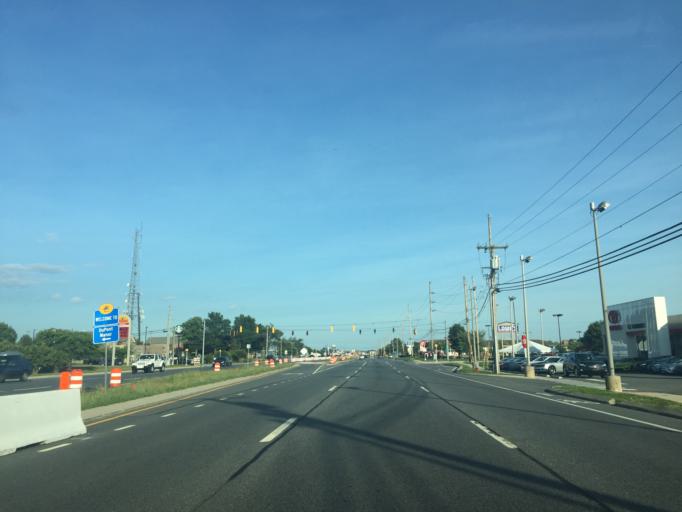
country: US
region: Delaware
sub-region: Kent County
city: Dover
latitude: 39.1948
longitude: -75.5487
